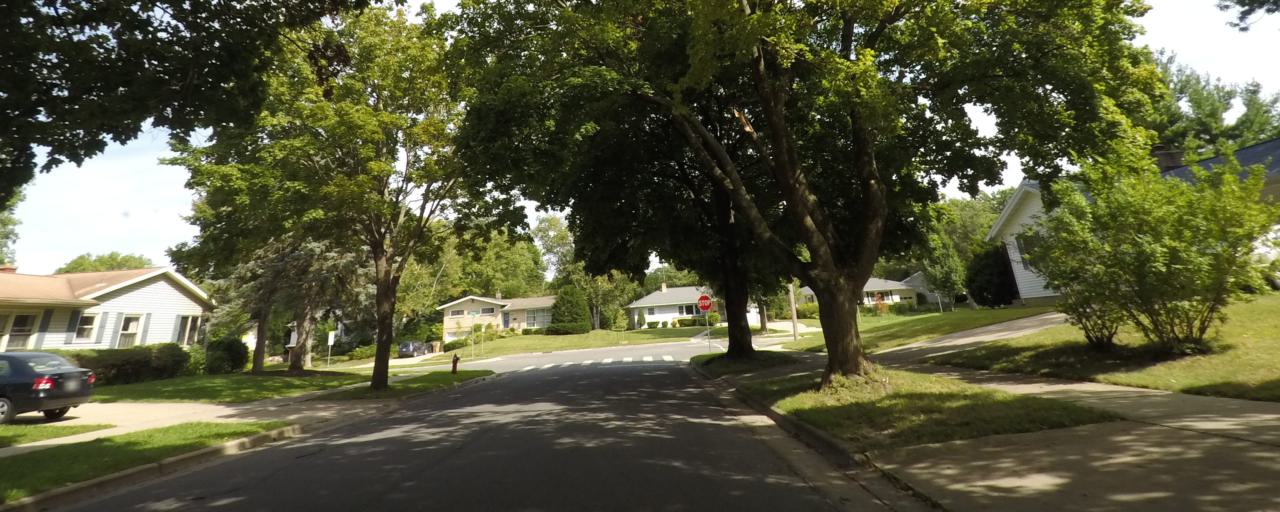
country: US
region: Wisconsin
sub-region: Dane County
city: Shorewood Hills
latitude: 43.0631
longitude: -89.4590
